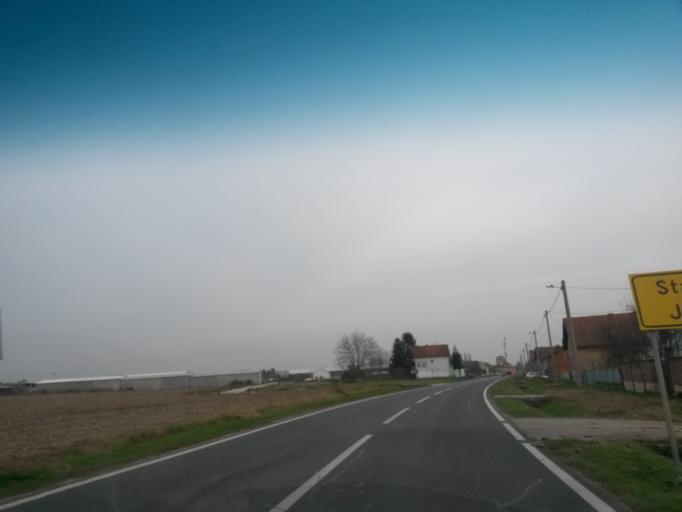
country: HR
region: Vukovarsko-Srijemska
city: Mirkovci
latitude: 45.2533
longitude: 18.8996
